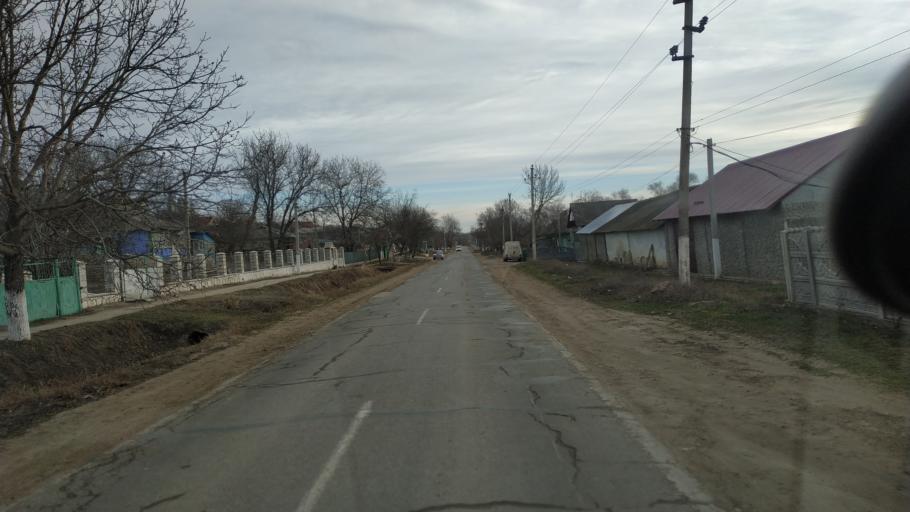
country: MD
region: Chisinau
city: Vadul lui Voda
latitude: 47.1406
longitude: 29.0638
